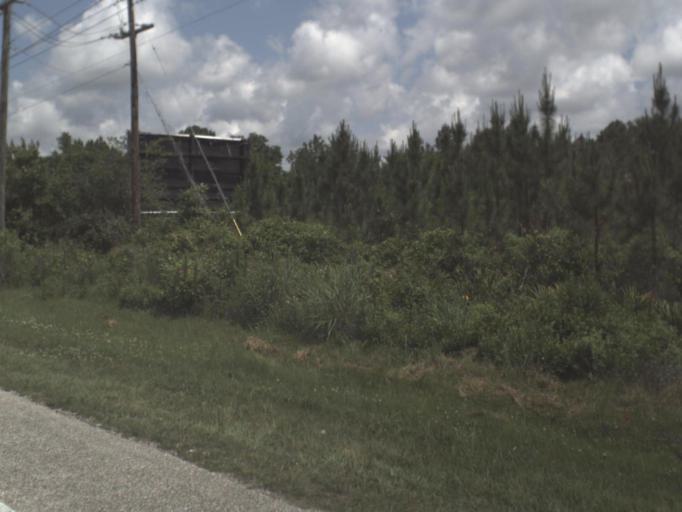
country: US
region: Florida
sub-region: Saint Johns County
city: Palm Valley
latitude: 30.0813
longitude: -81.4551
